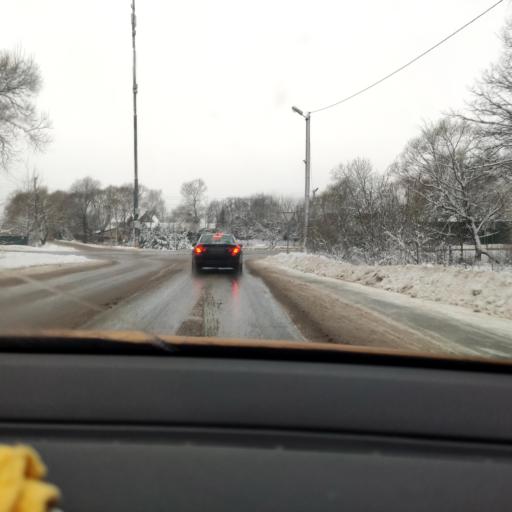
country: RU
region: Moskovskaya
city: Yershovo
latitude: 55.7636
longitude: 36.8597
